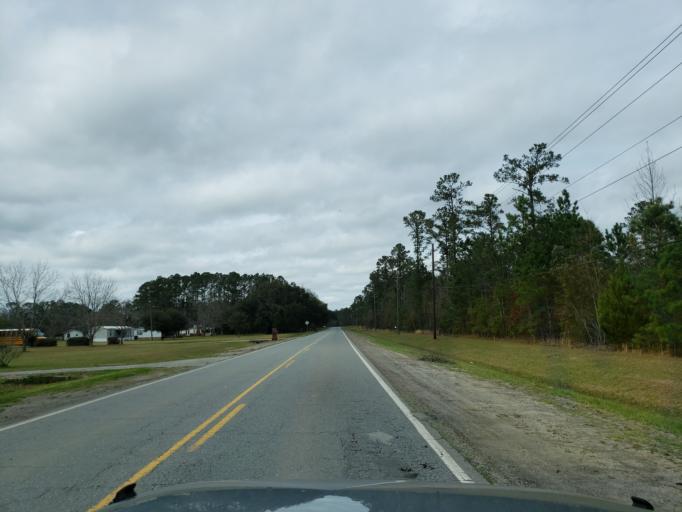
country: US
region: Georgia
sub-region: Chatham County
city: Georgetown
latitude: 32.0200
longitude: -81.2638
